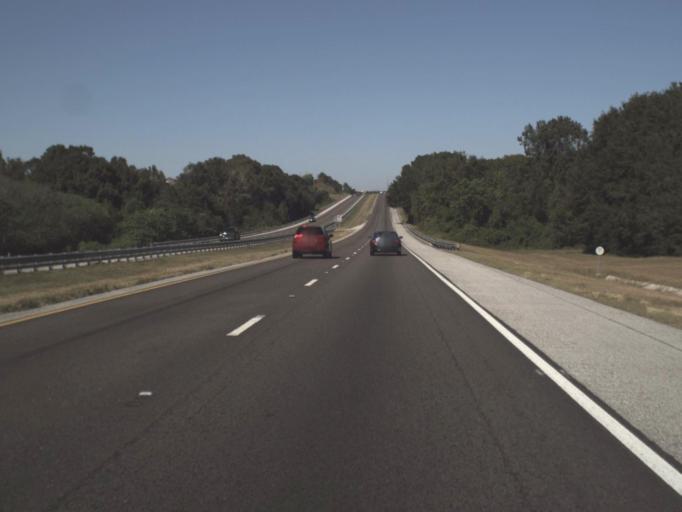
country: US
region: Florida
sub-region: Lake County
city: Montverde
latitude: 28.5651
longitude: -81.6875
